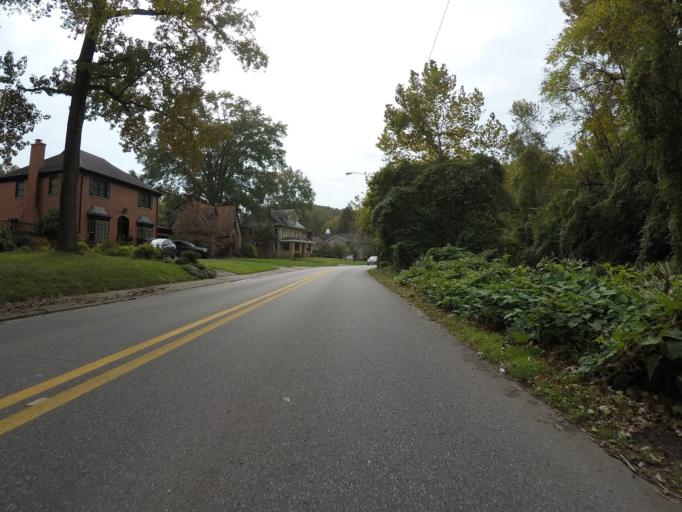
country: US
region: West Virginia
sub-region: Cabell County
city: Huntington
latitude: 38.4065
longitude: -82.4320
